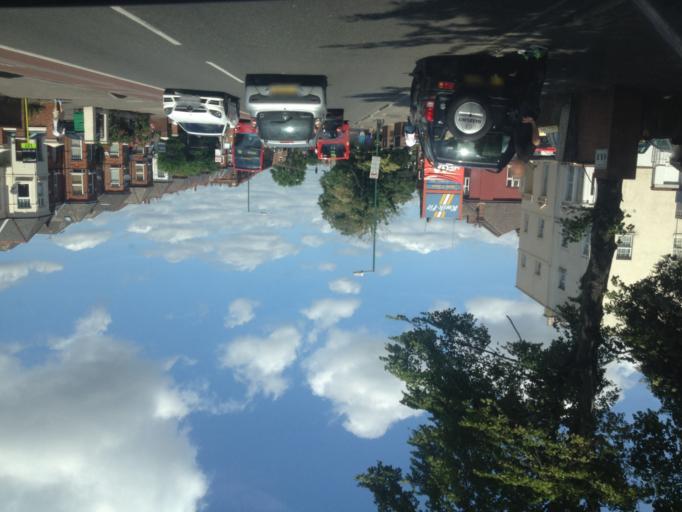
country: GB
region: England
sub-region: Greater London
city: Belsize Park
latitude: 51.5513
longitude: -0.2088
